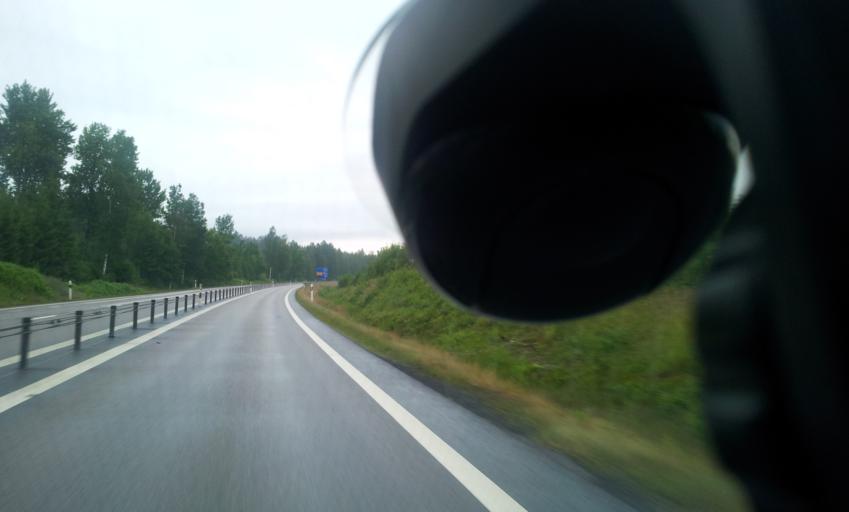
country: SE
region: Kalmar
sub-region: Vasterviks Kommun
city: Forserum
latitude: 58.0475
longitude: 16.5240
